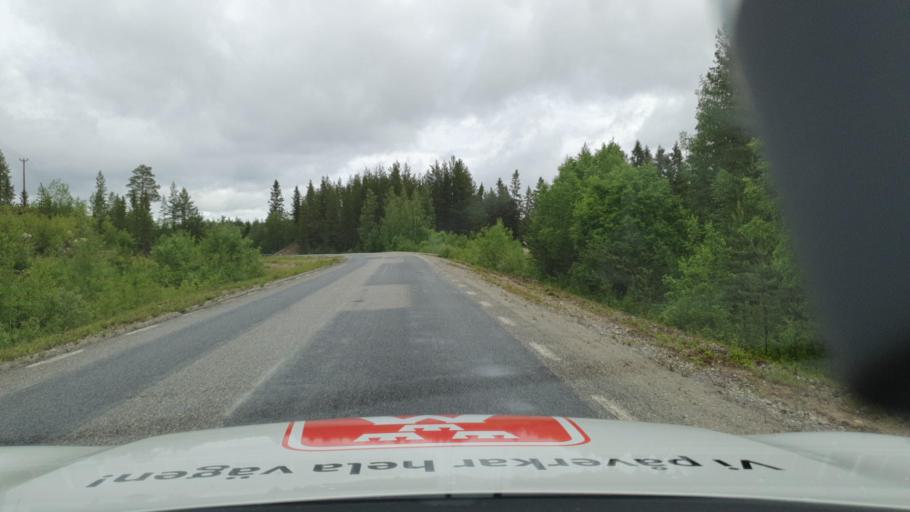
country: SE
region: Vaesterbotten
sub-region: Dorotea Kommun
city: Dorotea
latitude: 64.1386
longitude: 16.6430
